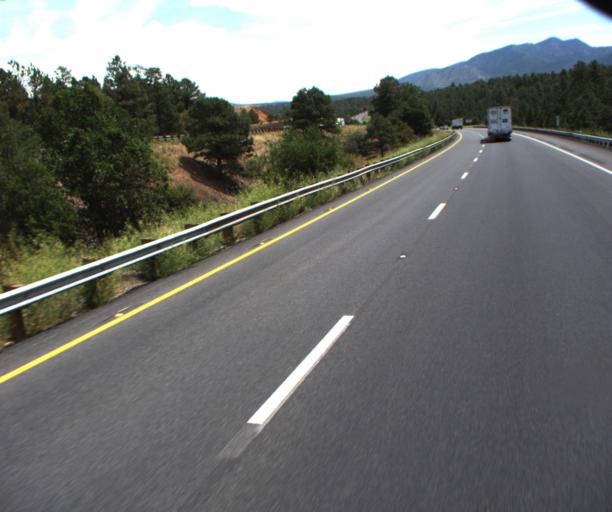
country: US
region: Arizona
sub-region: Coconino County
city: Williams
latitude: 35.2197
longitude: -112.3081
